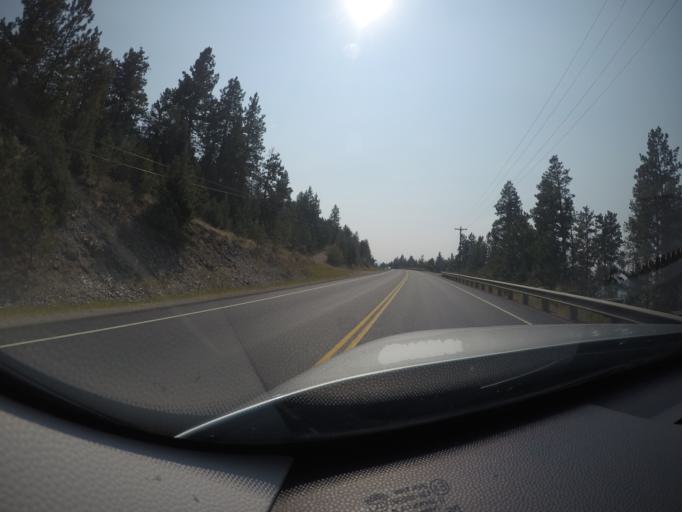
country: US
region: Montana
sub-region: Lake County
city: Polson
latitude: 47.8097
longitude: -114.2680
